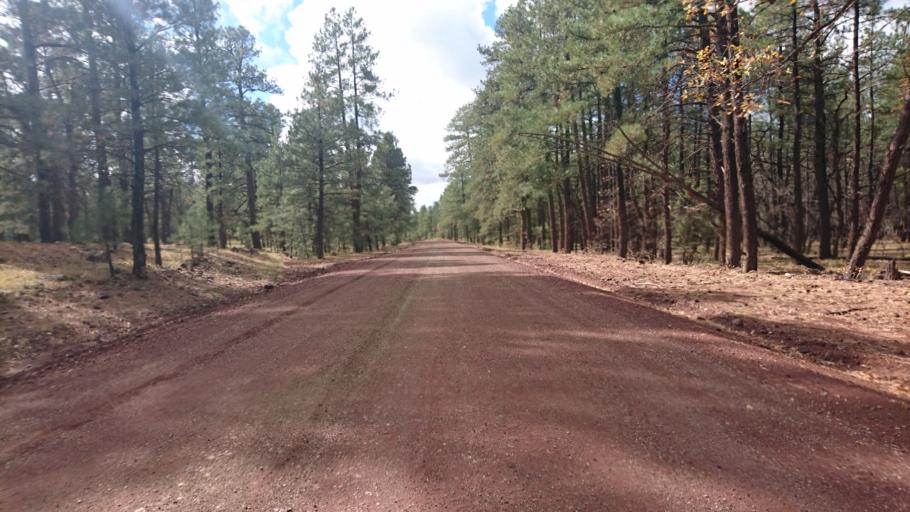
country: US
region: Arizona
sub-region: Coconino County
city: Parks
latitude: 35.2713
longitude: -111.9083
